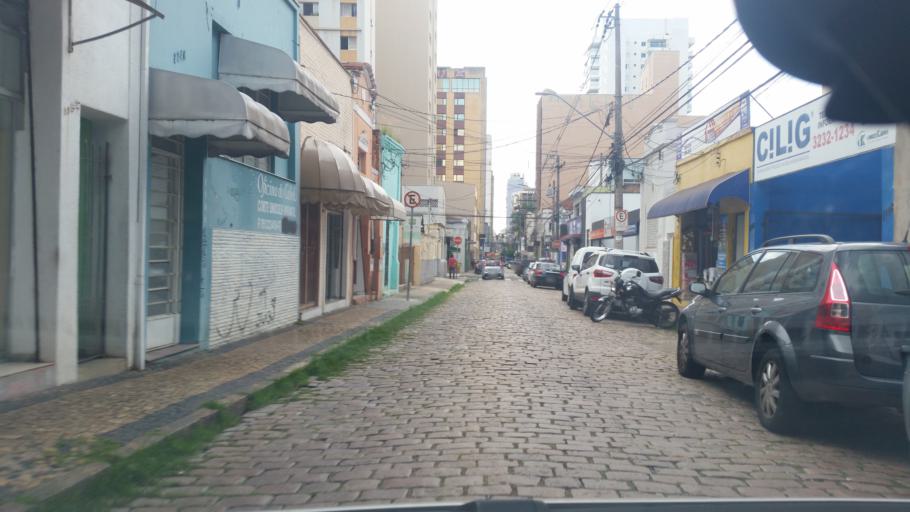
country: BR
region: Sao Paulo
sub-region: Campinas
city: Campinas
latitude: -22.9046
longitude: -47.0546
